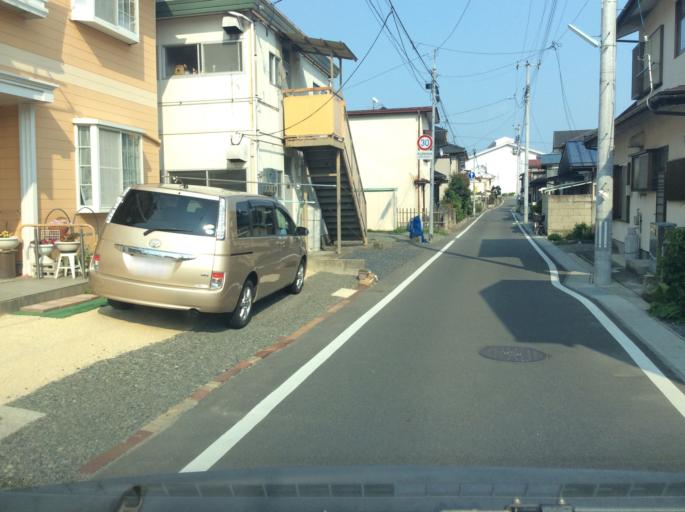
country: JP
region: Fukushima
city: Sukagawa
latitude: 37.1241
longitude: 140.2180
